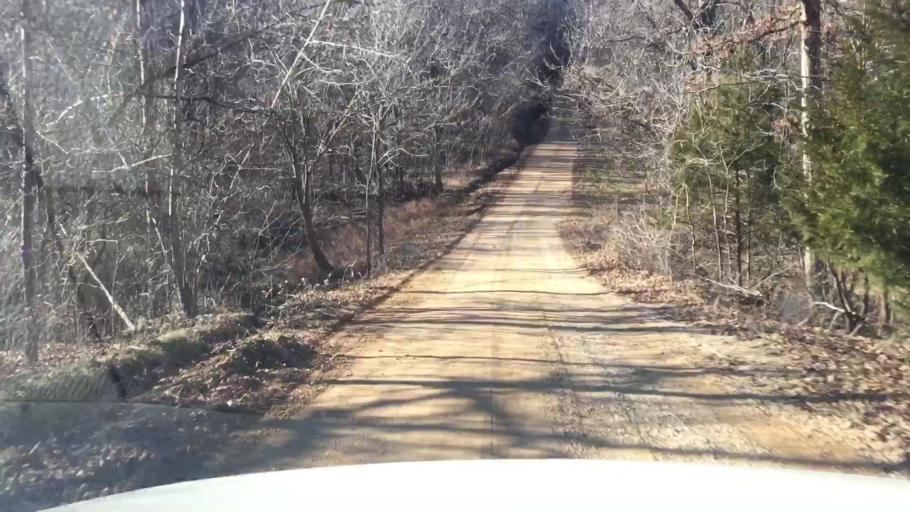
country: US
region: Missouri
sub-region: Morgan County
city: Versailles
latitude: 38.3241
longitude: -92.7655
